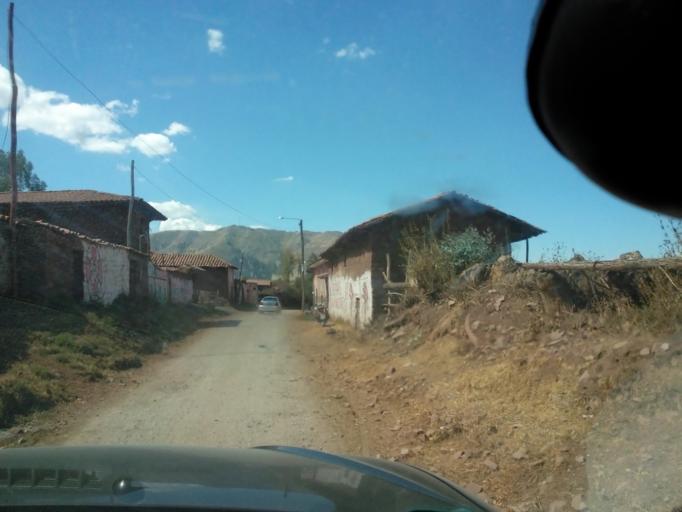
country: PE
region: Cusco
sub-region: Provincia de Anta
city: Zurite
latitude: -13.4369
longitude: -72.2314
